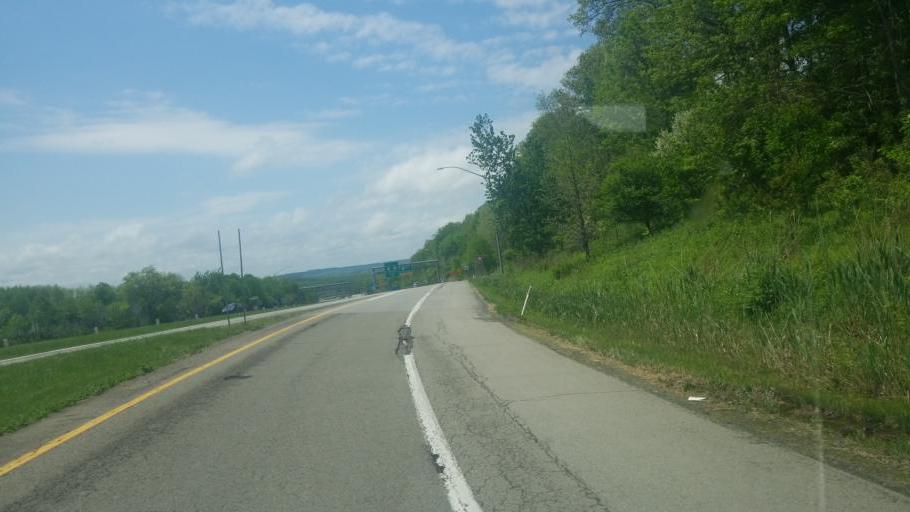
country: US
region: Pennsylvania
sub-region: Mercer County
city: Hermitage
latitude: 41.1868
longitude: -80.4460
